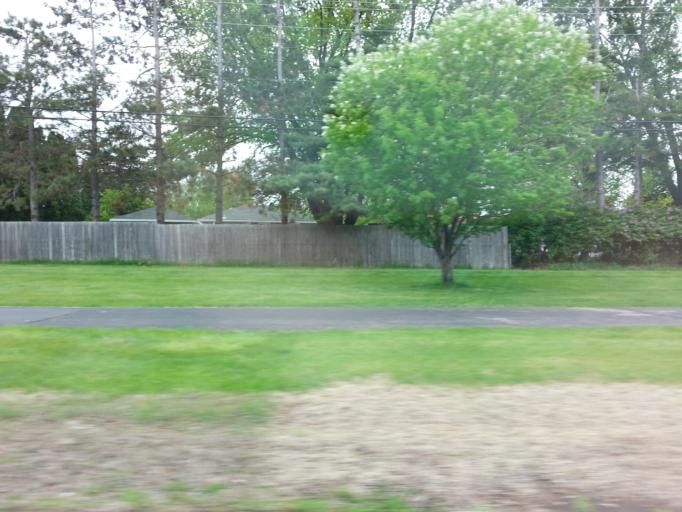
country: US
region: Minnesota
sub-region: Washington County
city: Oakdale
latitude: 44.9683
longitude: -92.9647
